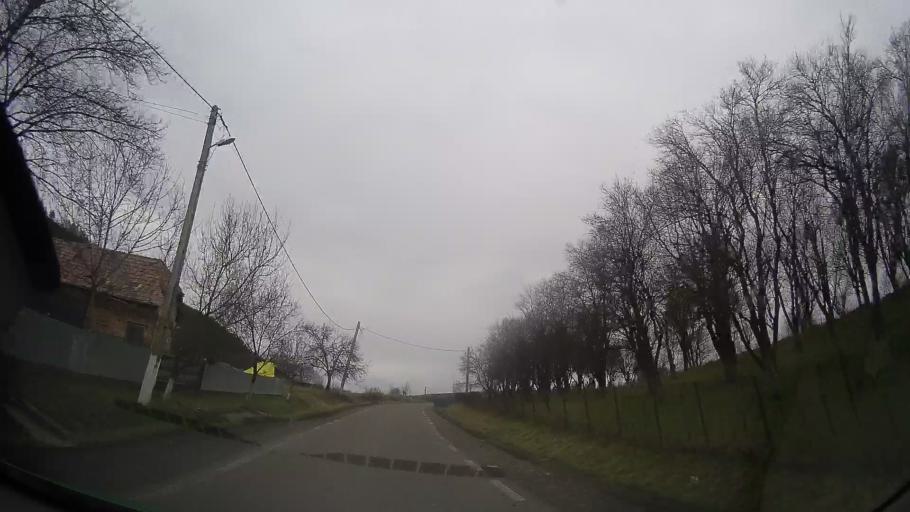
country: RO
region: Mures
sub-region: Comuna Bala
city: Bala
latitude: 46.7151
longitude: 24.5043
